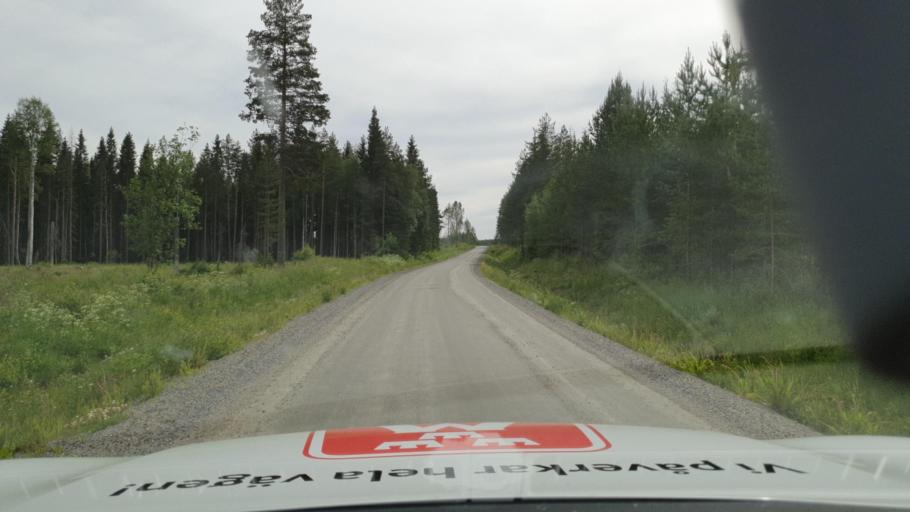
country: SE
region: Vaesterbotten
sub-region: Skelleftea Kommun
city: Burea
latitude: 64.4205
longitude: 21.0093
